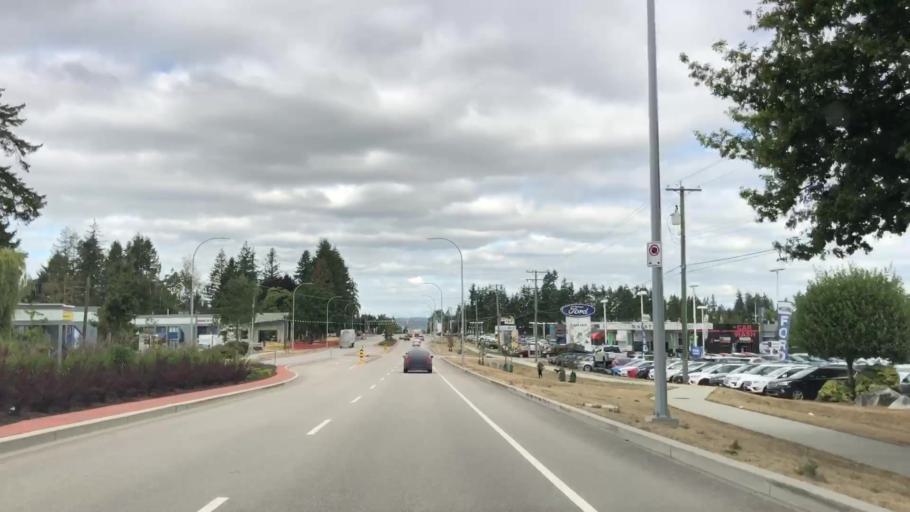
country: CA
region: British Columbia
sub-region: Greater Vancouver Regional District
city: White Rock
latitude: 49.0562
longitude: -122.8065
